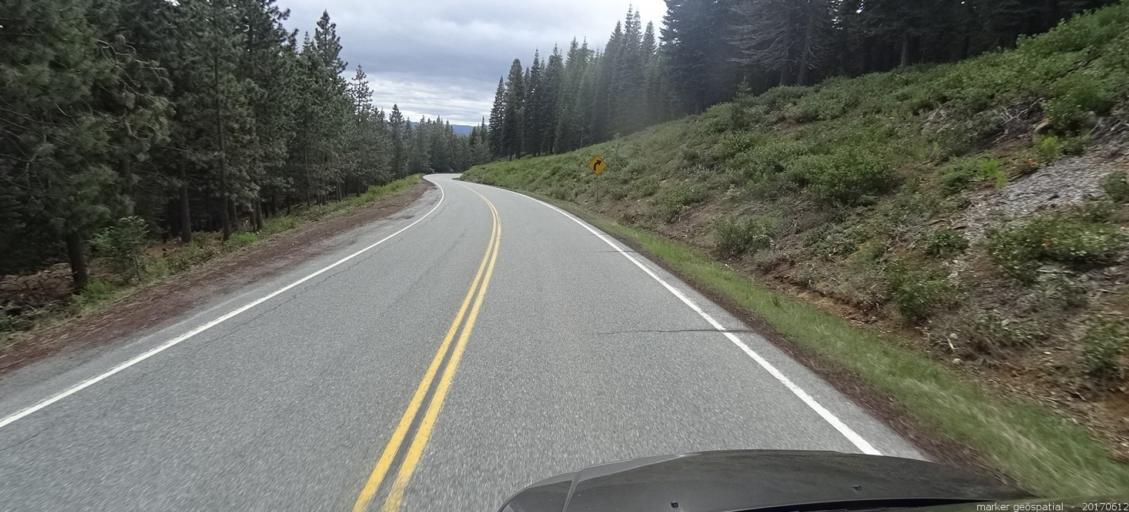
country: US
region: California
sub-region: Siskiyou County
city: Mount Shasta
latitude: 41.3304
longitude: -122.2499
